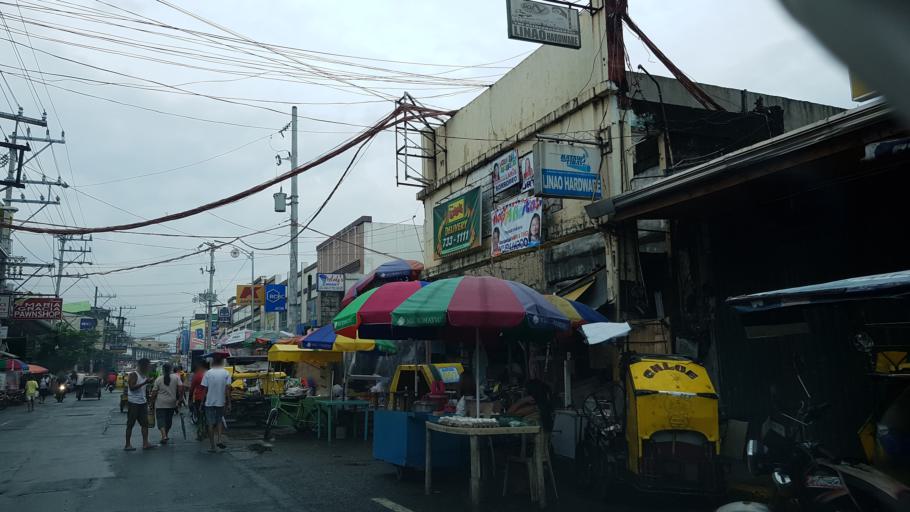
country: PH
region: Metro Manila
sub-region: City of Manila
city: Quiapo
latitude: 14.5764
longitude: 120.9939
